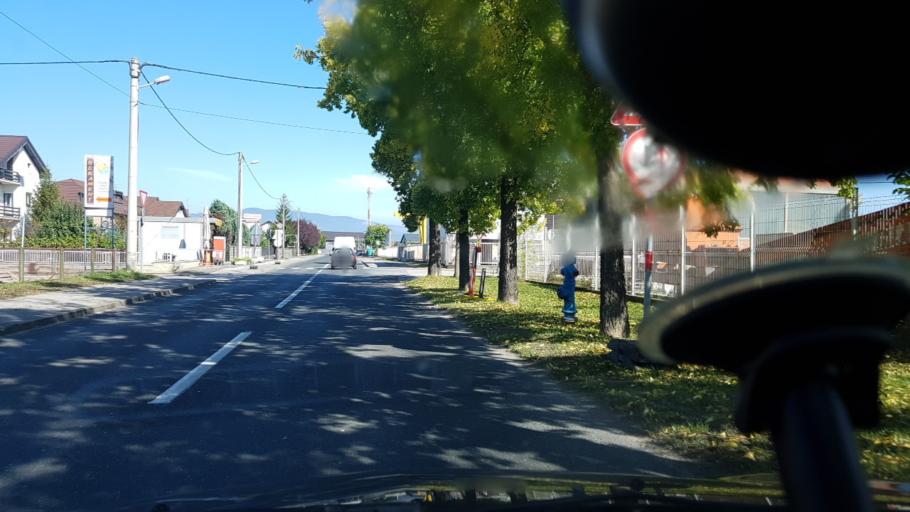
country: HR
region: Grad Zagreb
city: Lucko
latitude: 45.7578
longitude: 15.8924
